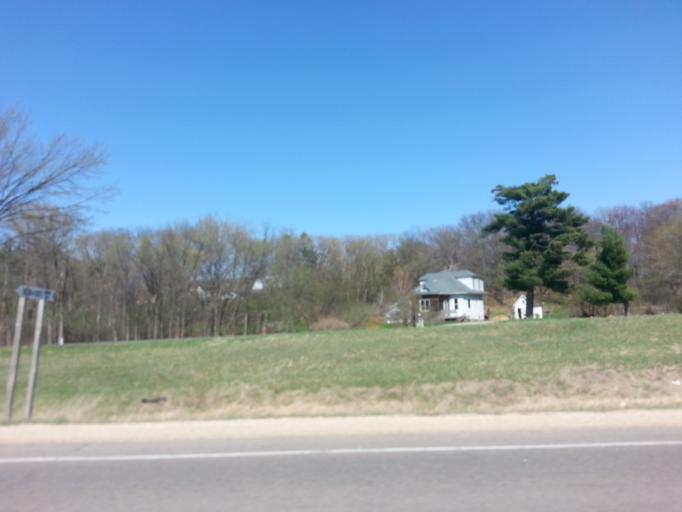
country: US
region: Wisconsin
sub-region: Dunn County
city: Menomonie
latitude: 44.8808
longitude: -91.9464
